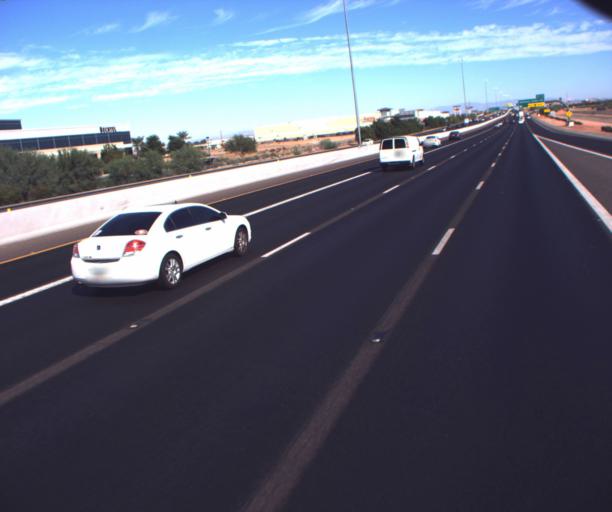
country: US
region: Arizona
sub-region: Maricopa County
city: Tolleson
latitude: 33.5125
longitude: -112.2690
